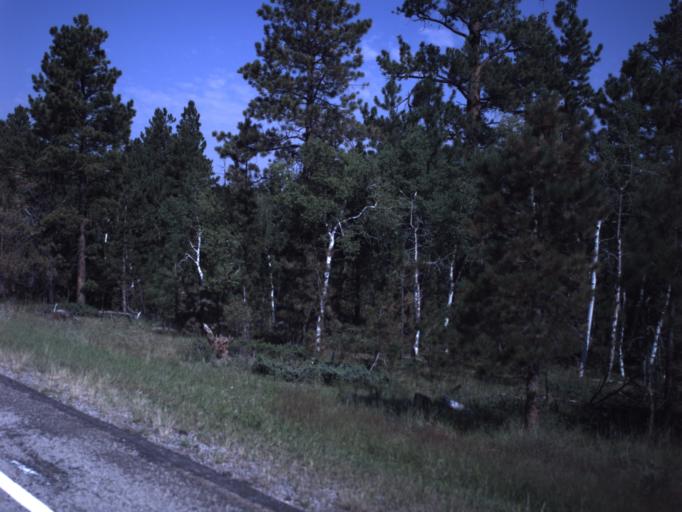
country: US
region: Utah
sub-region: Daggett County
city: Manila
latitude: 40.8519
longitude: -109.6132
